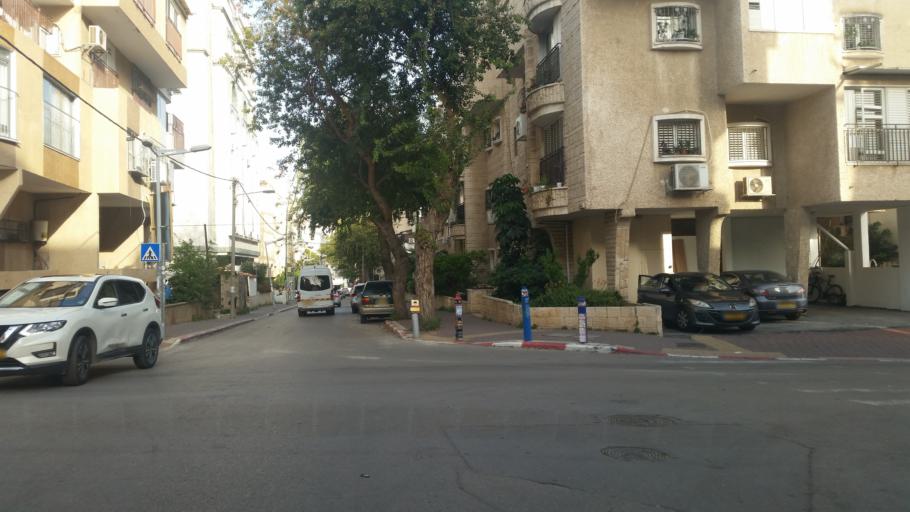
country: IL
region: Tel Aviv
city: Bene Beraq
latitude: 32.0745
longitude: 34.8394
